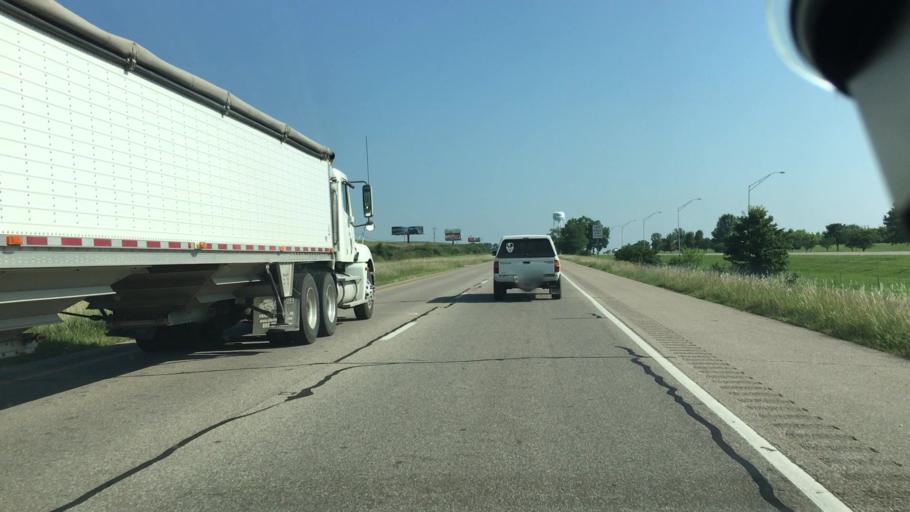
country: US
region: Indiana
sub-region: Gibson County
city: Fort Branch
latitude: 38.2809
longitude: -87.5676
